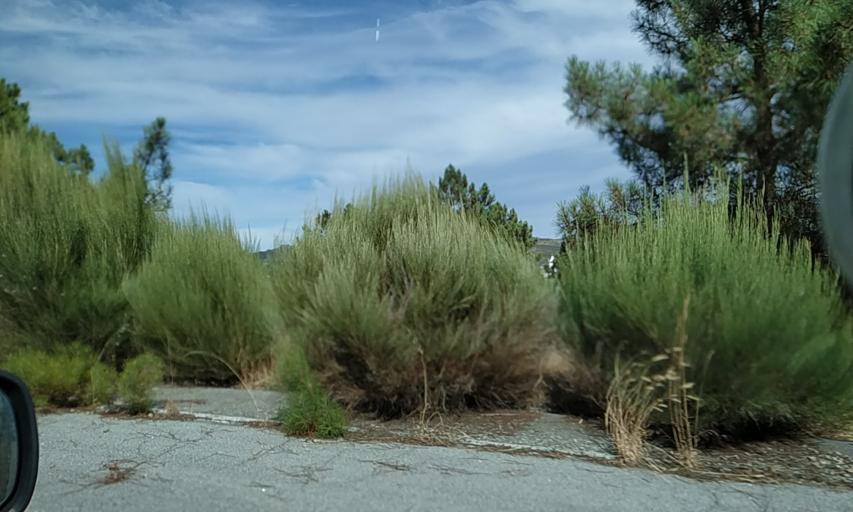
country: PT
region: Vila Real
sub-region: Sabrosa
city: Sabrosa
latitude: 41.3645
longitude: -7.5539
